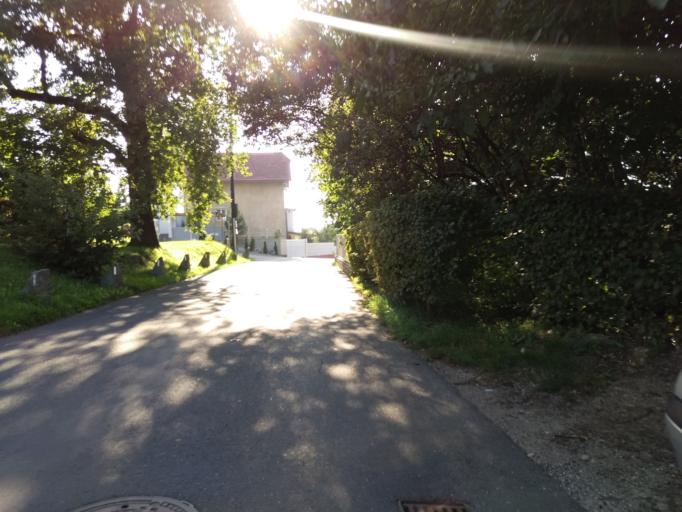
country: AT
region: Styria
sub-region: Graz Stadt
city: Graz
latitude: 47.0736
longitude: 15.4743
